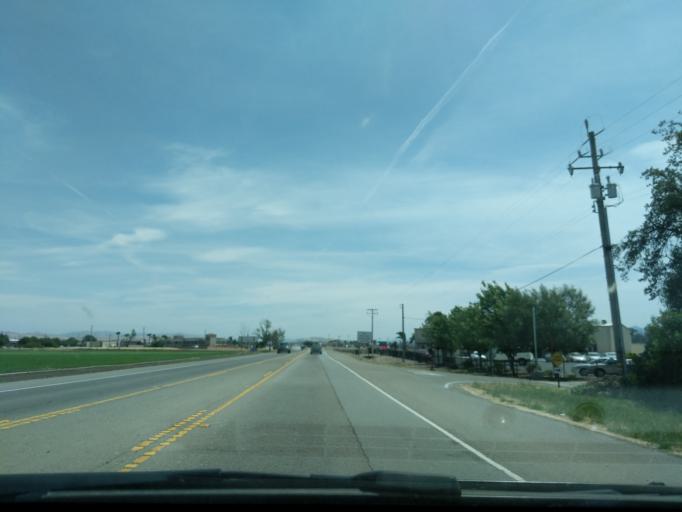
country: US
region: California
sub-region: San Benito County
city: Hollister
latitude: 36.8686
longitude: -121.4055
